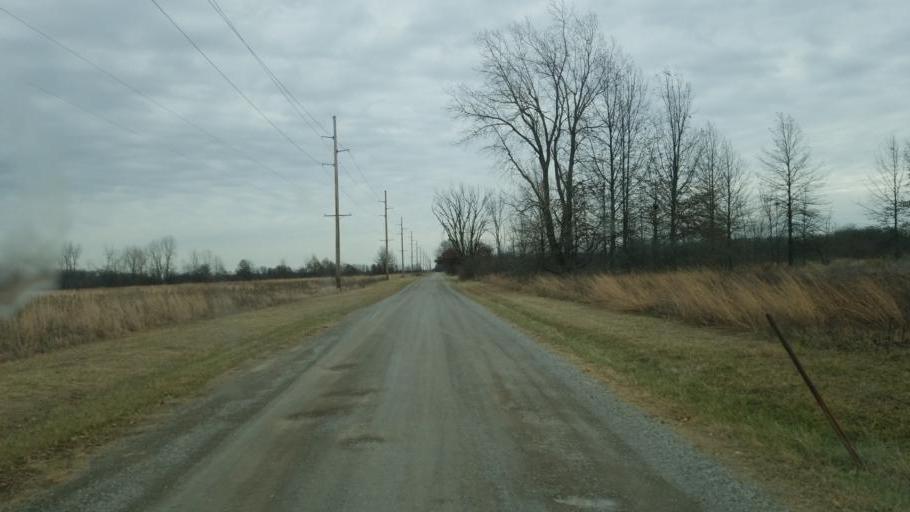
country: US
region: Ohio
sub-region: Wyandot County
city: Upper Sandusky
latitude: 40.7240
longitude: -83.2974
